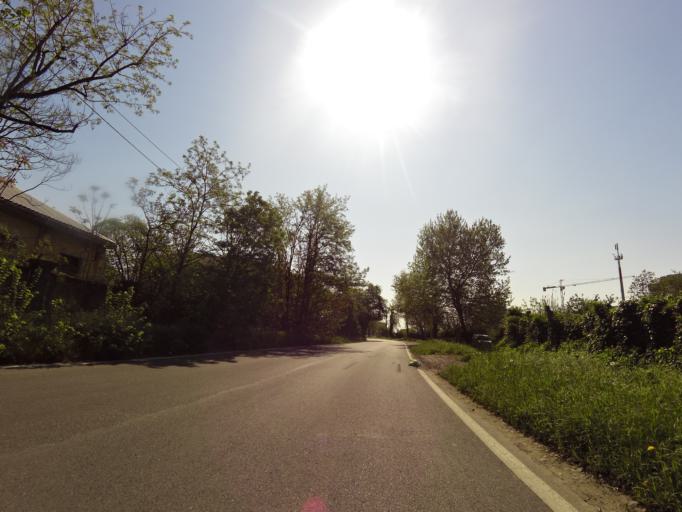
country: IT
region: Lombardy
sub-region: Citta metropolitana di Milano
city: Chiaravalle
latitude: 45.4451
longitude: 9.2375
